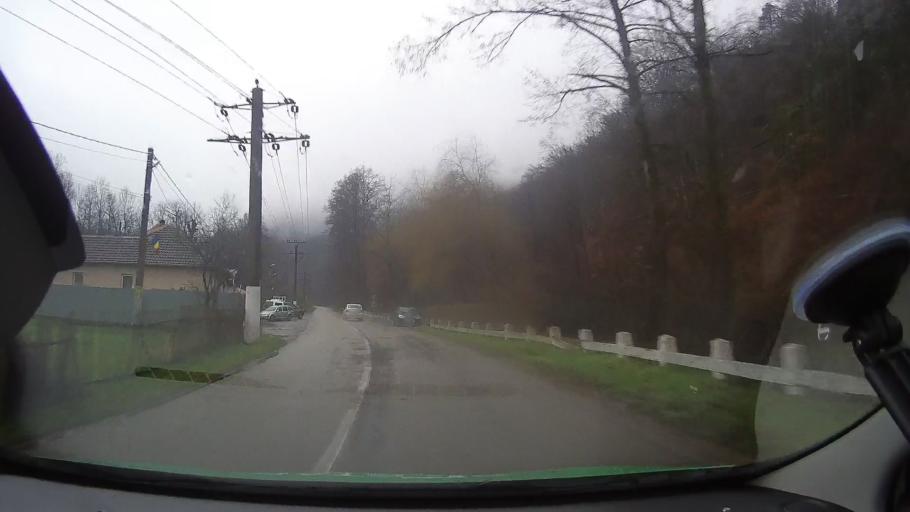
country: RO
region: Arad
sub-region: Comuna Dezna
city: Dezna
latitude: 46.4142
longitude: 22.2548
